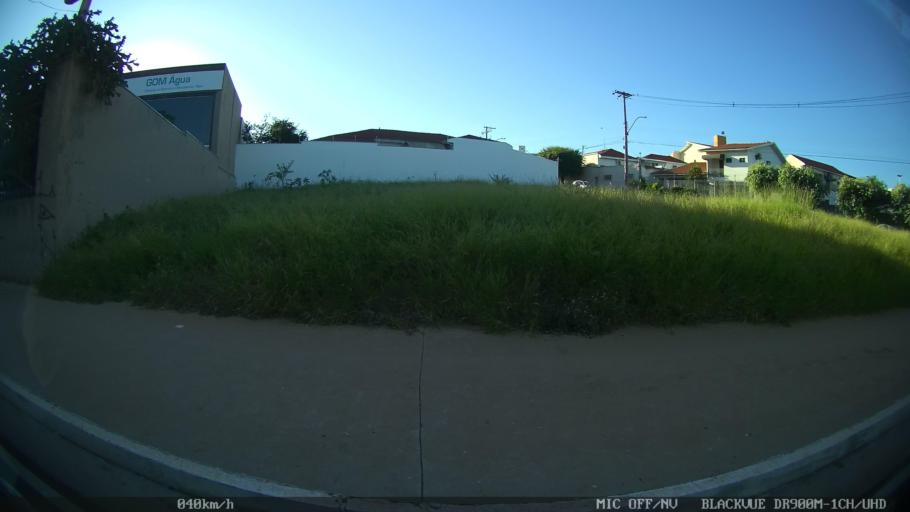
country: BR
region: Sao Paulo
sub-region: Sao Jose Do Rio Preto
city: Sao Jose do Rio Preto
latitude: -20.8085
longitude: -49.3716
